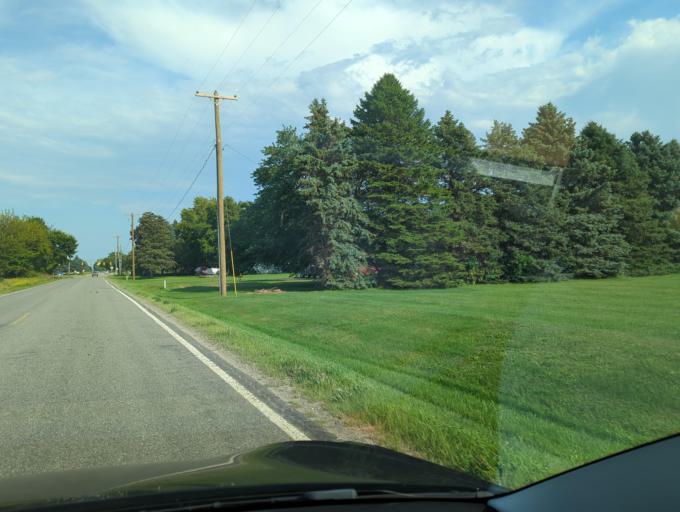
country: US
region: Michigan
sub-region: Ionia County
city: Ionia
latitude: 42.9296
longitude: -85.0783
